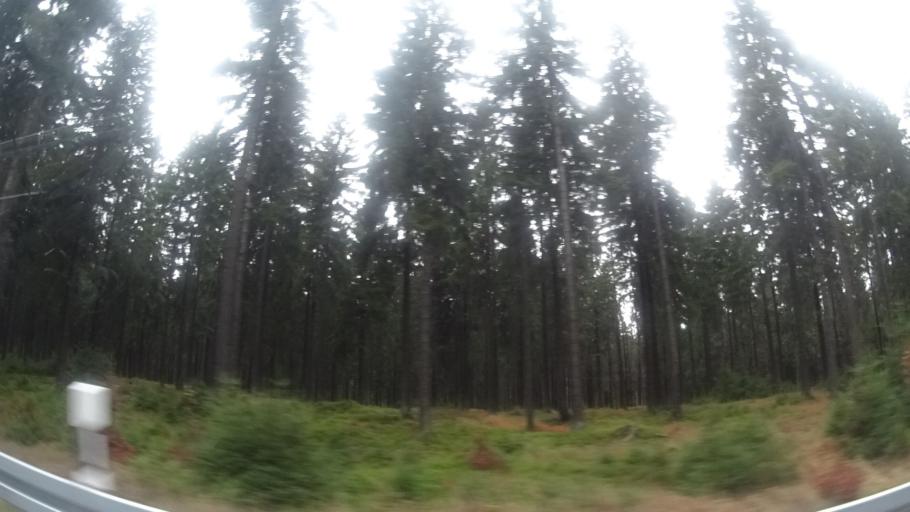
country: DE
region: Thuringia
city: Steinheid
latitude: 50.4943
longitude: 11.1041
